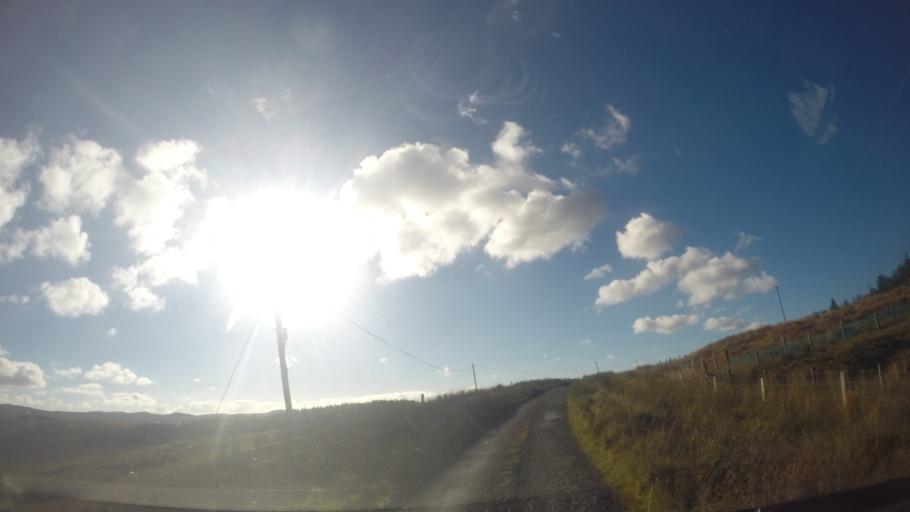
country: IE
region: Ulster
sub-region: County Donegal
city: Killybegs
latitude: 54.7226
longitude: -8.5698
